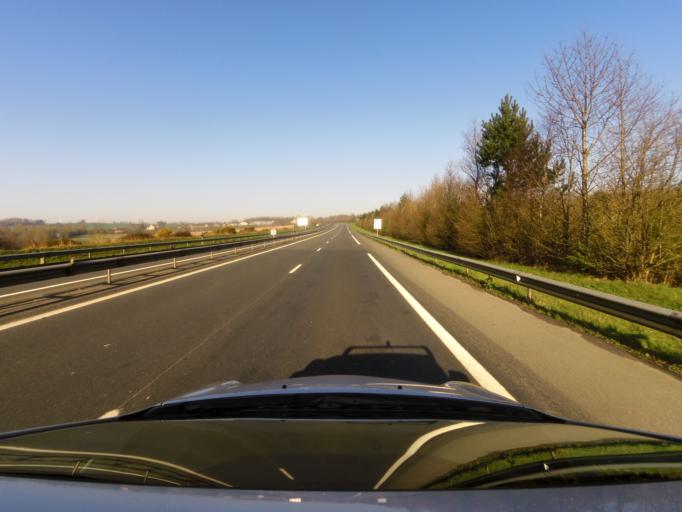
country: FR
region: Lower Normandy
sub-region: Departement du Calvados
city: Cahagnes
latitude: 49.0508
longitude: -0.7373
